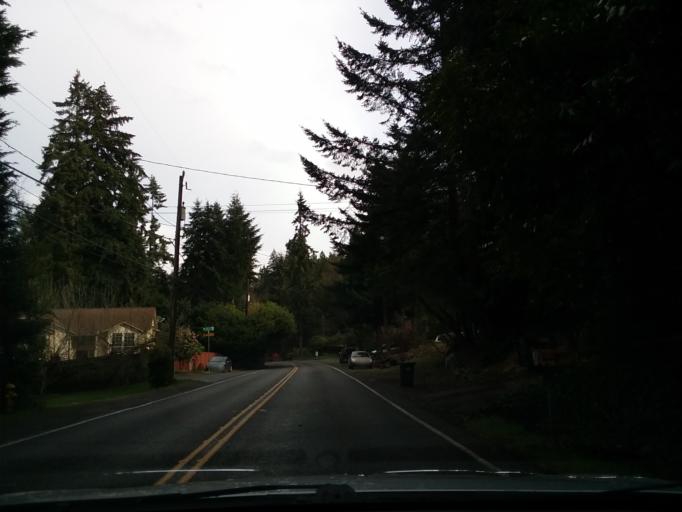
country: US
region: Washington
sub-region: Snohomish County
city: Mountlake Terrace
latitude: 47.7600
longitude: -122.3090
